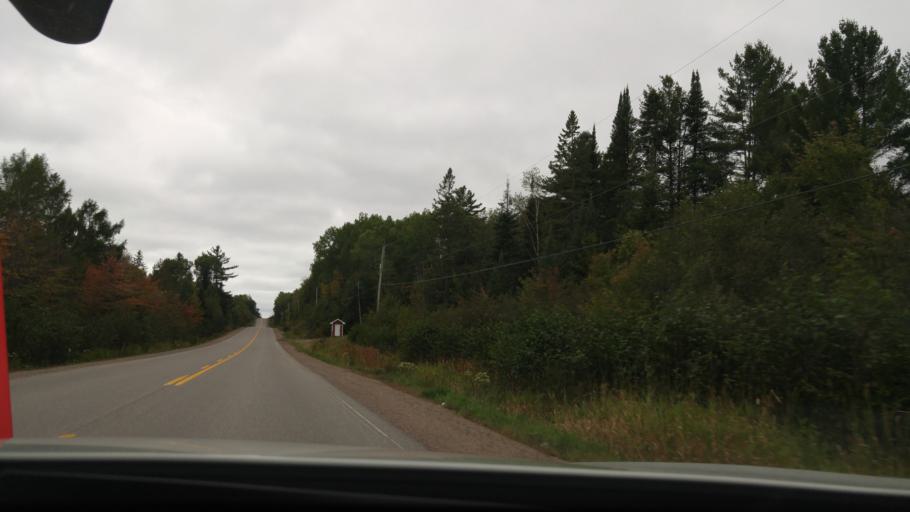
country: CA
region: Ontario
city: Petawawa
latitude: 45.8271
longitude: -77.2815
